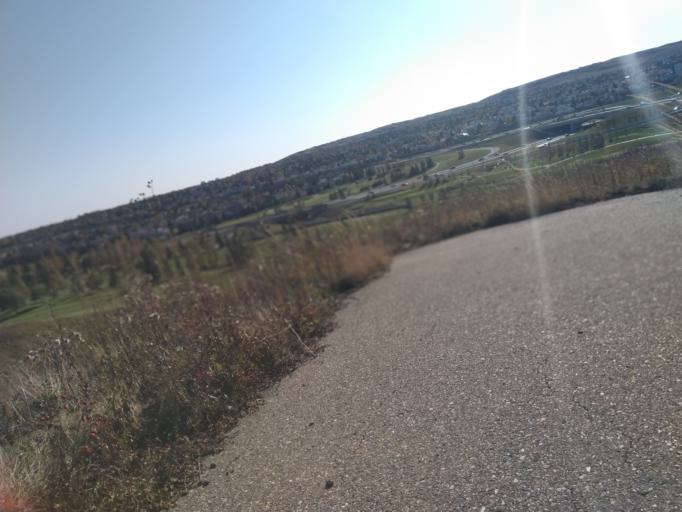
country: CA
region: Alberta
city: Calgary
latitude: 51.1482
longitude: -114.0886
